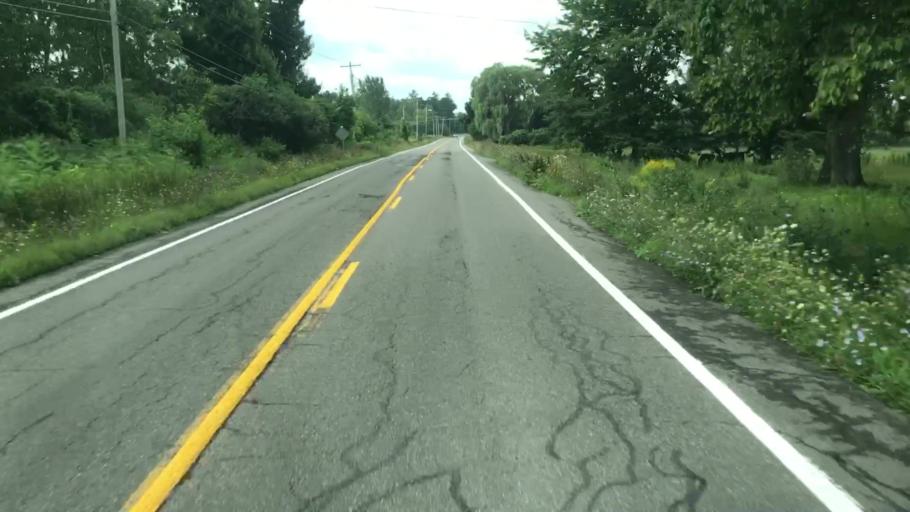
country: US
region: New York
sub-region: Onondaga County
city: Skaneateles
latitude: 42.9684
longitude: -76.4303
